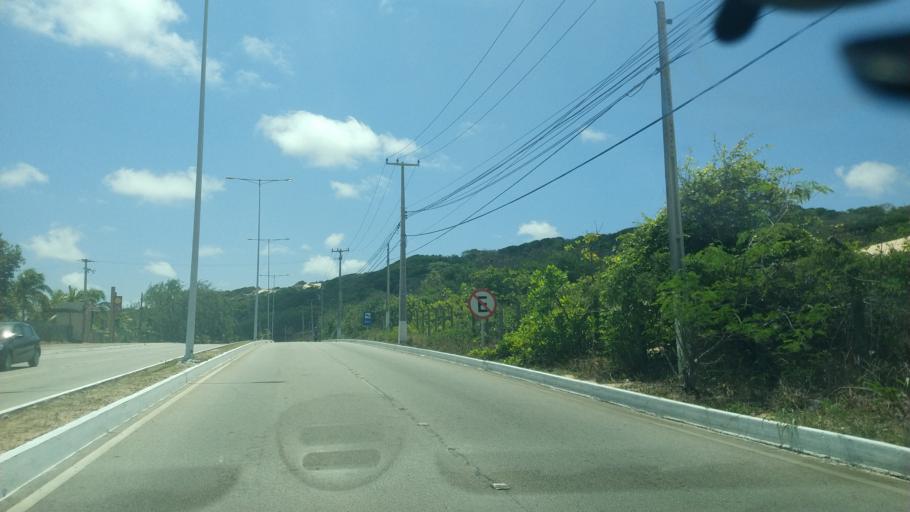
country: BR
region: Rio Grande do Norte
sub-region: Natal
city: Natal
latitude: -5.8060
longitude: -35.1823
